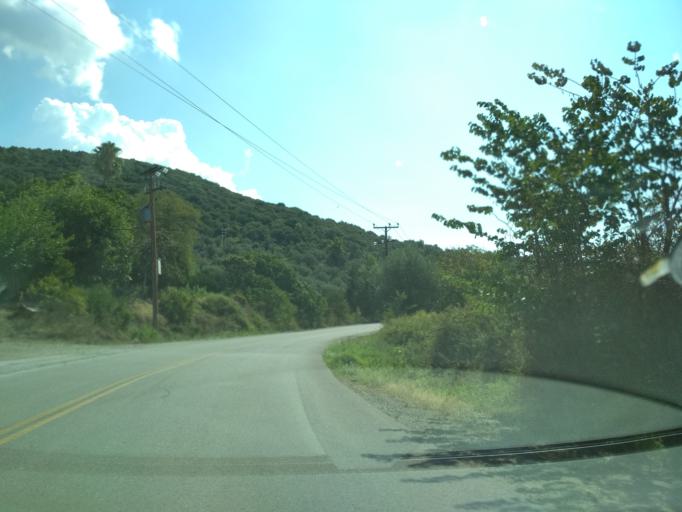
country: GR
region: Central Greece
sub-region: Nomos Evvoias
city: Roviai
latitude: 38.8414
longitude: 23.1734
